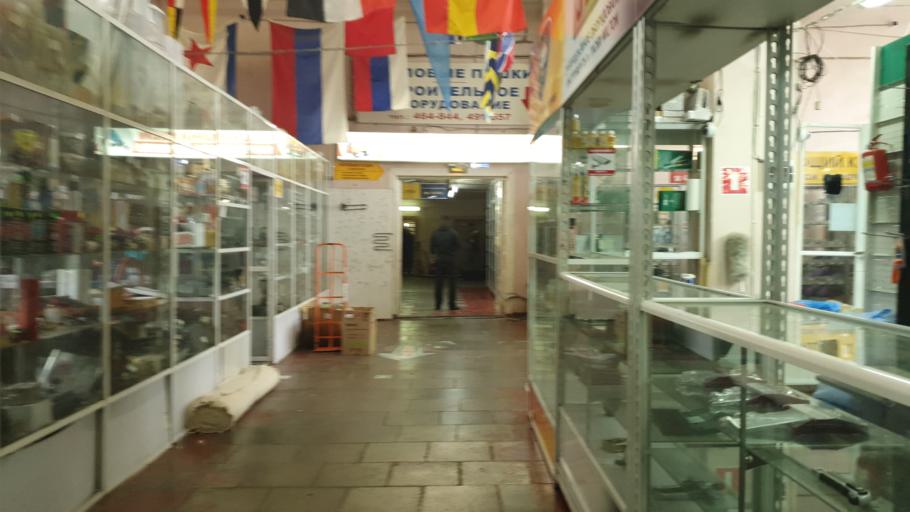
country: RU
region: Primorskiy
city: Vladivostok
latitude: 43.1116
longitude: 131.9150
